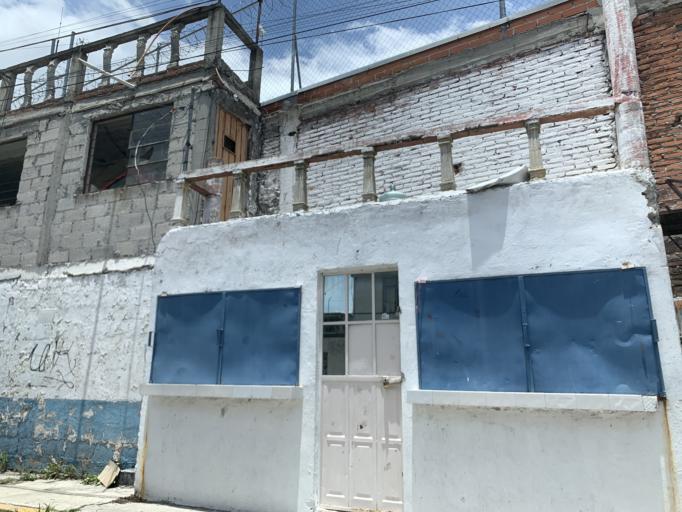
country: MX
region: Puebla
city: Puebla
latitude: 19.0673
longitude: -98.2050
